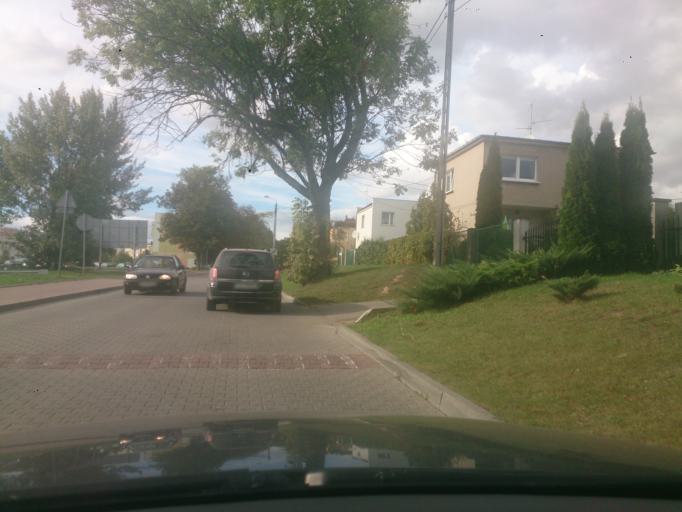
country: PL
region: Kujawsko-Pomorskie
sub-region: Grudziadz
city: Grudziadz
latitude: 53.4629
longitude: 18.7328
